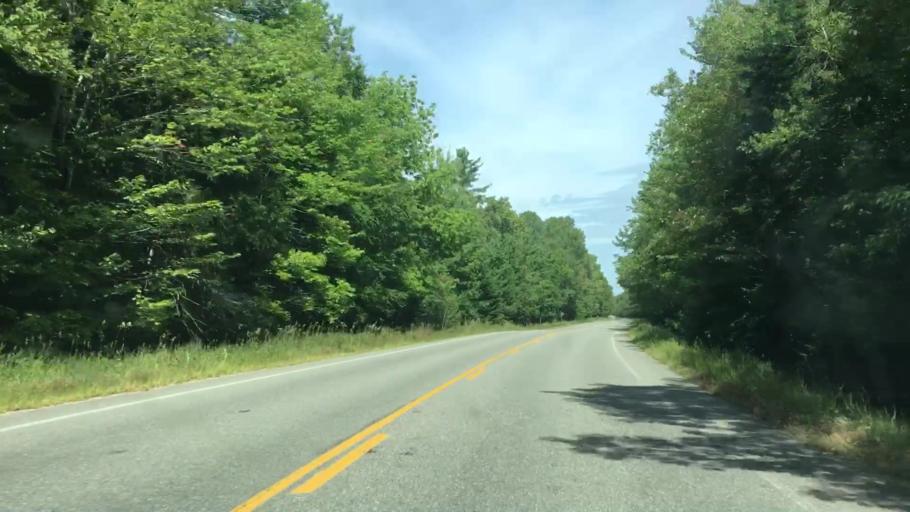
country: US
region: Maine
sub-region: Penobscot County
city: Lincoln
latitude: 45.3797
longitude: -68.5481
